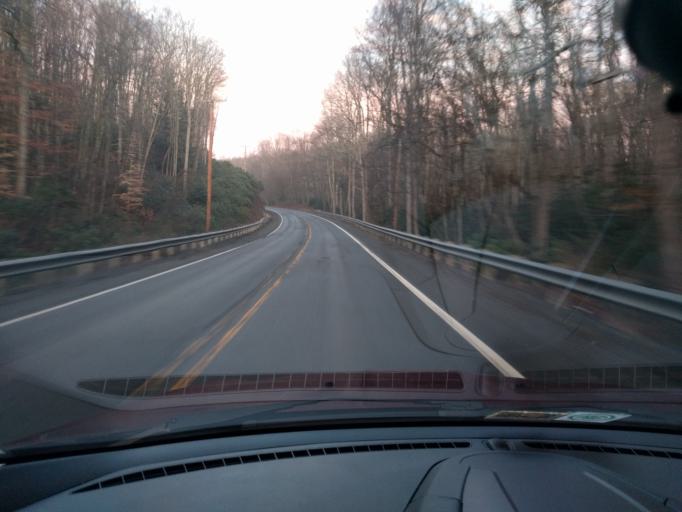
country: US
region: West Virginia
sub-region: Fayette County
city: Fayetteville
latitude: 38.0488
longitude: -80.9422
